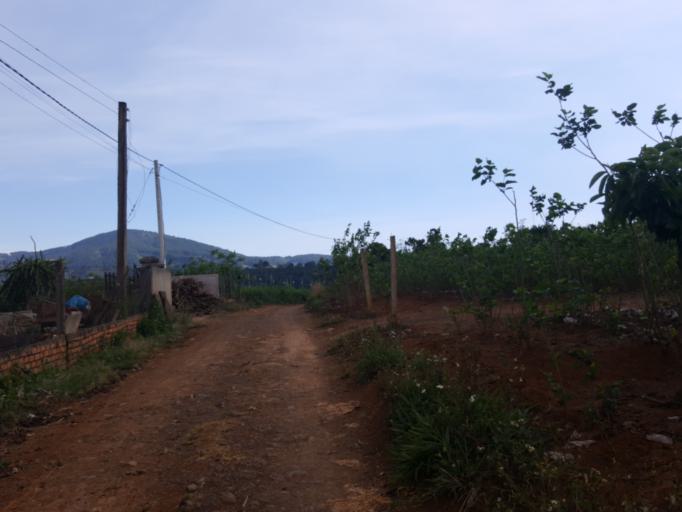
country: VN
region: Lam Dong
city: Duc Trong
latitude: 11.8379
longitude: 108.3482
